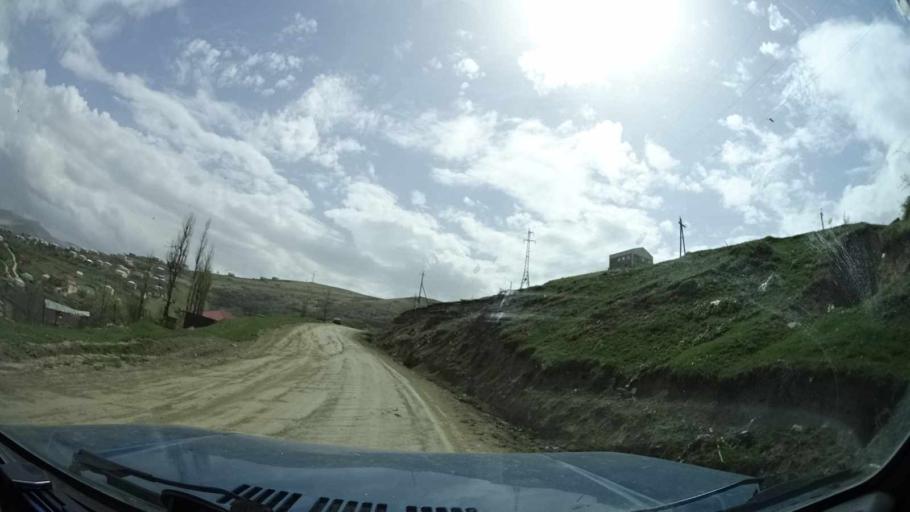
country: RU
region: Dagestan
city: Kubachi
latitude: 42.0945
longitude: 47.5929
